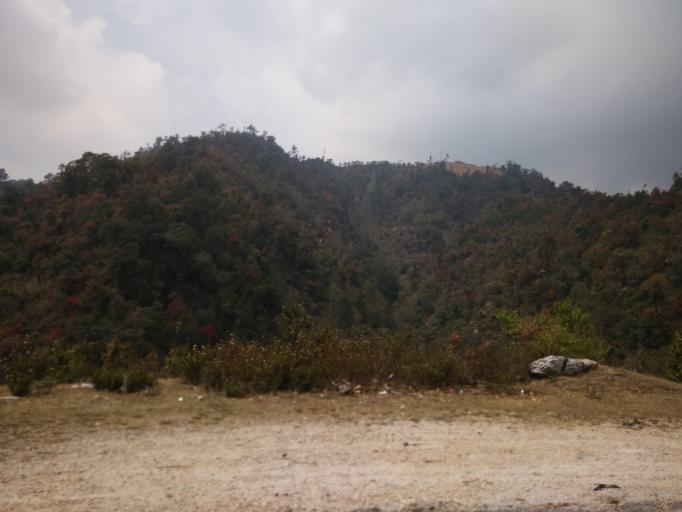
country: NP
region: Central Region
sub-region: Narayani Zone
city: Hitura
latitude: 27.5728
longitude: 85.0751
